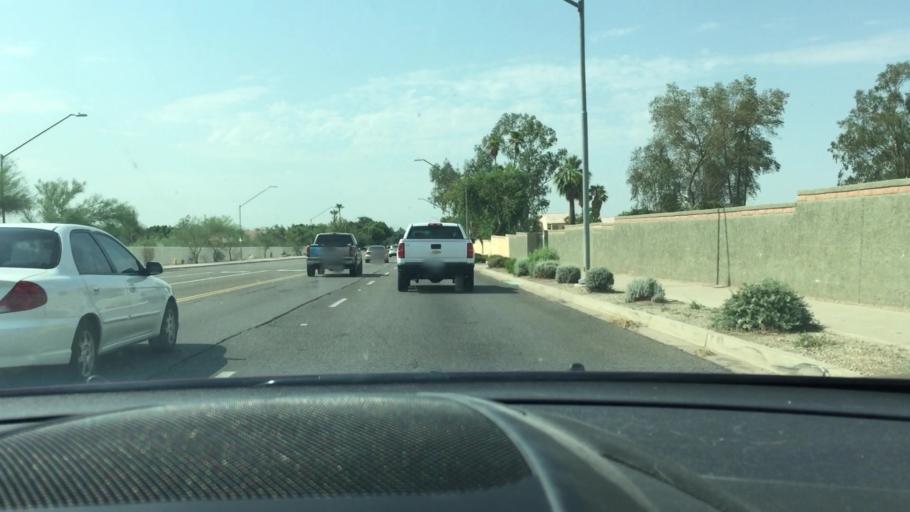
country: US
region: Arizona
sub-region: Maricopa County
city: Peoria
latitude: 33.6889
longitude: -112.2032
